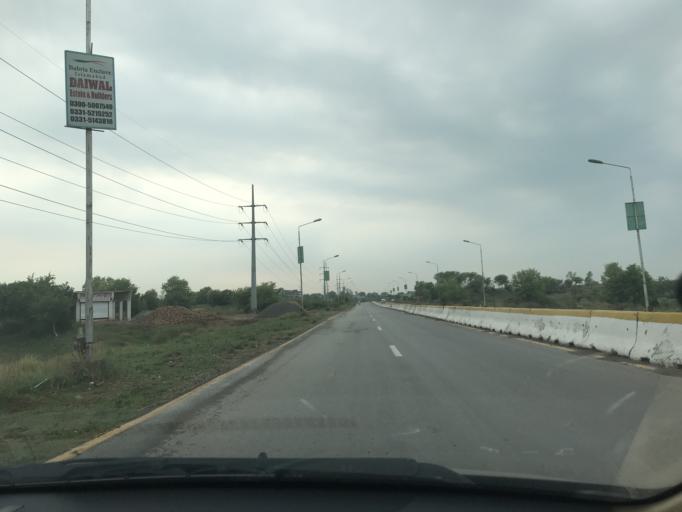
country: PK
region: Islamabad
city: Islamabad
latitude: 33.6973
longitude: 73.1804
